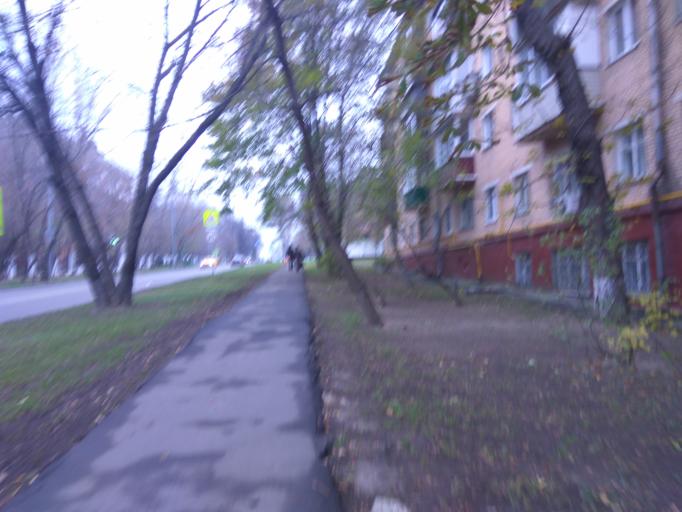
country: RU
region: Moscow
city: Tsaritsyno
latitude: 55.6422
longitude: 37.6714
